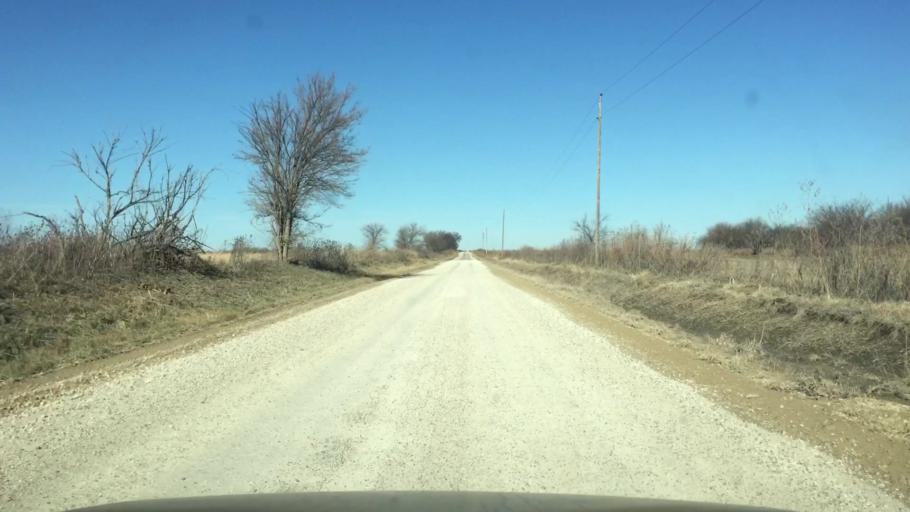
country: US
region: Kansas
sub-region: Allen County
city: Humboldt
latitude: 37.8518
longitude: -95.3909
